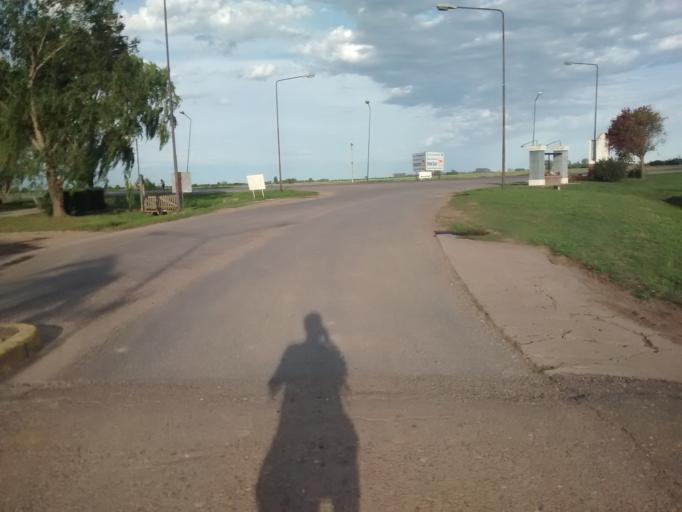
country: AR
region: Santa Fe
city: Galvez
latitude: -31.9037
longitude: -61.2735
